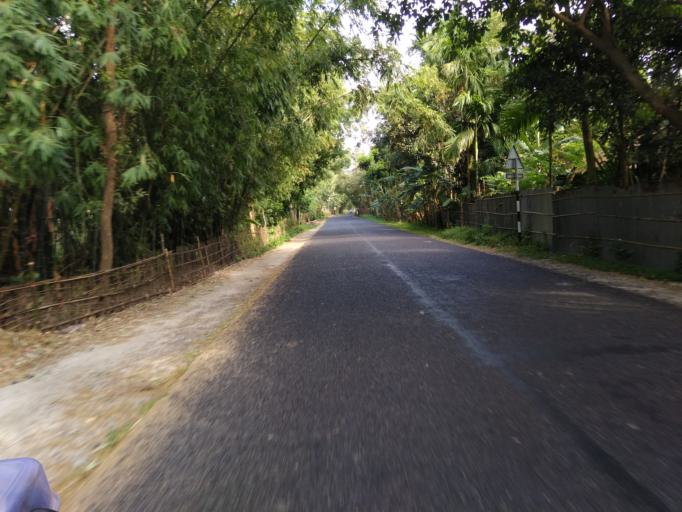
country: BD
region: Rangpur Division
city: Rangpur
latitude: 25.8364
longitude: 89.1149
